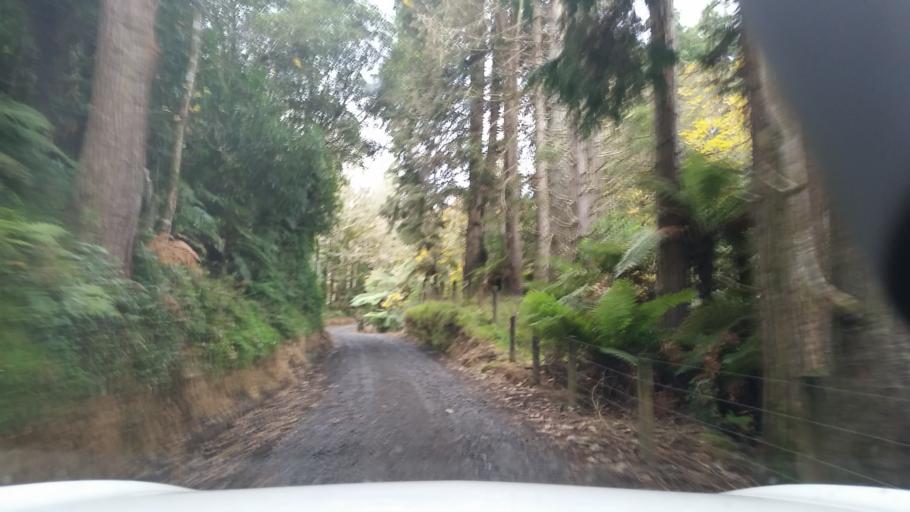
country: NZ
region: Taranaki
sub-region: New Plymouth District
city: Waitara
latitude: -39.1518
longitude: 174.5243
